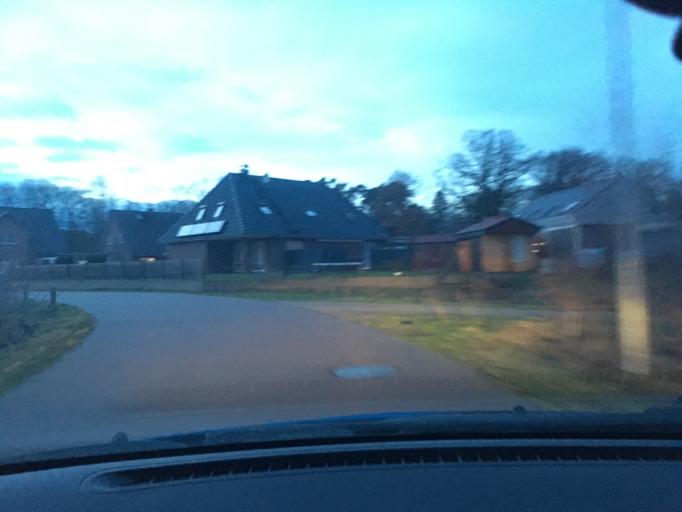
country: DE
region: Lower Saxony
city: Embsen
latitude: 53.1903
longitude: 10.3310
